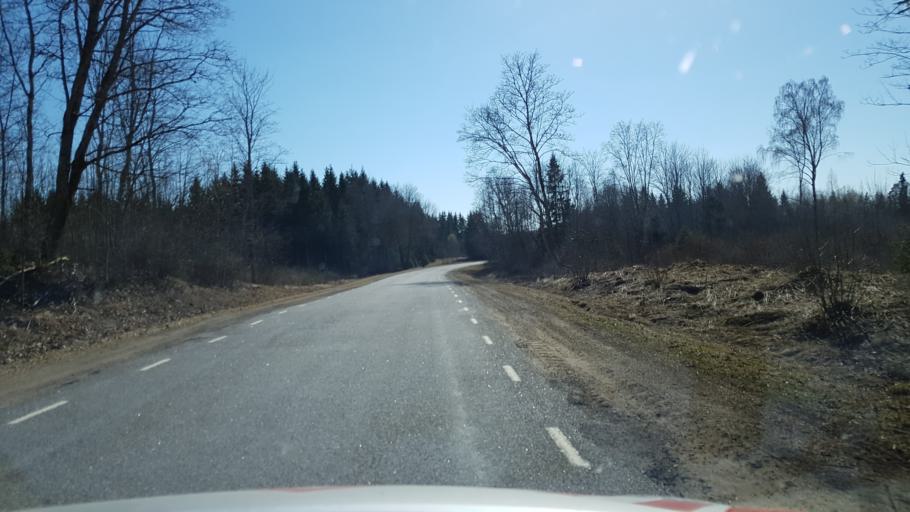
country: EE
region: Laeaene-Virumaa
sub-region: Tamsalu vald
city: Tamsalu
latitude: 59.0560
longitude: 26.1007
